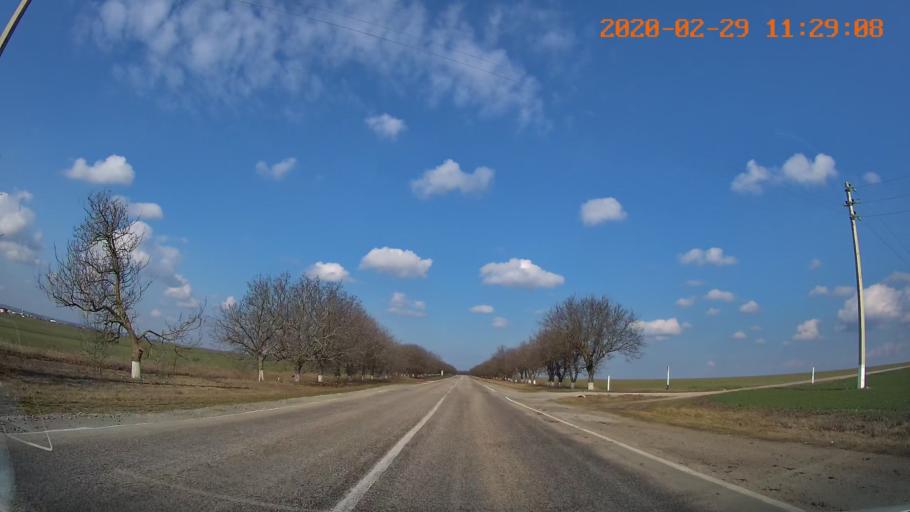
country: MD
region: Telenesti
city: Cocieri
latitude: 47.4898
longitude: 29.1281
